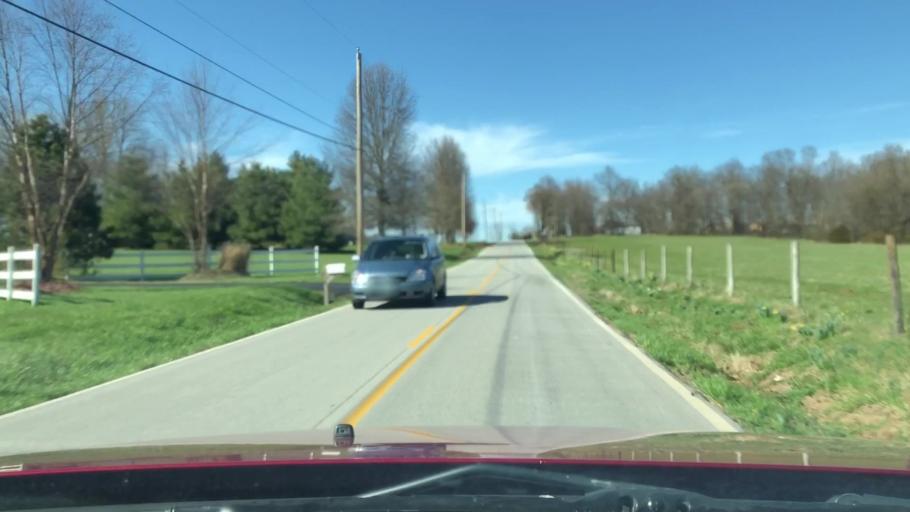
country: US
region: Missouri
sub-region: Greene County
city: Strafford
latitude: 37.2357
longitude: -93.1883
